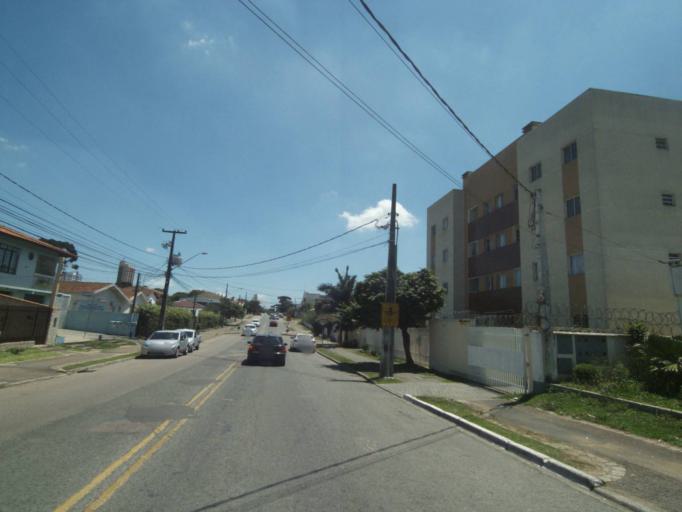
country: BR
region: Parana
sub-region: Curitiba
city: Curitiba
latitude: -25.3864
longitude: -49.2276
